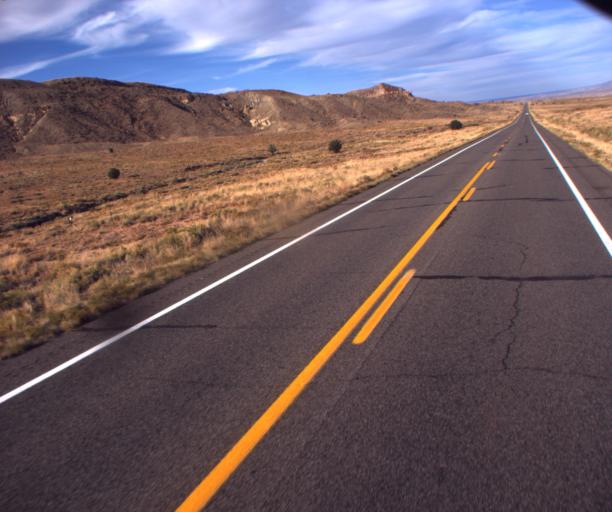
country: US
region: New Mexico
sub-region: San Juan County
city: Shiprock
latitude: 36.9305
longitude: -109.0804
